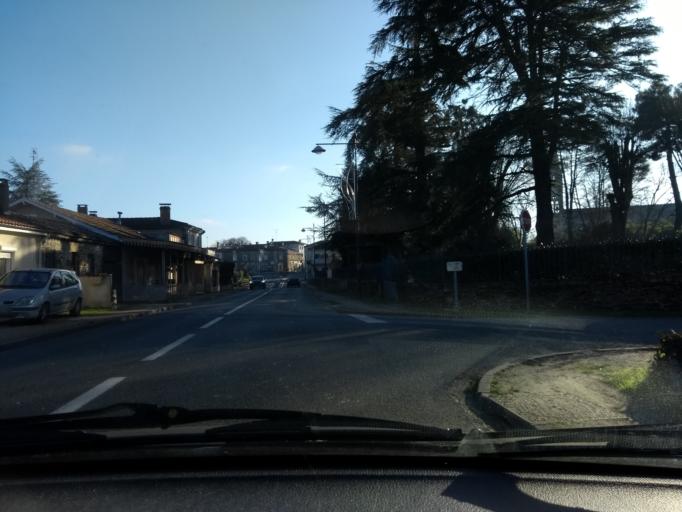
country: FR
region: Aquitaine
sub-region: Departement de la Gironde
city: Salles
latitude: 44.5535
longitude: -0.8705
